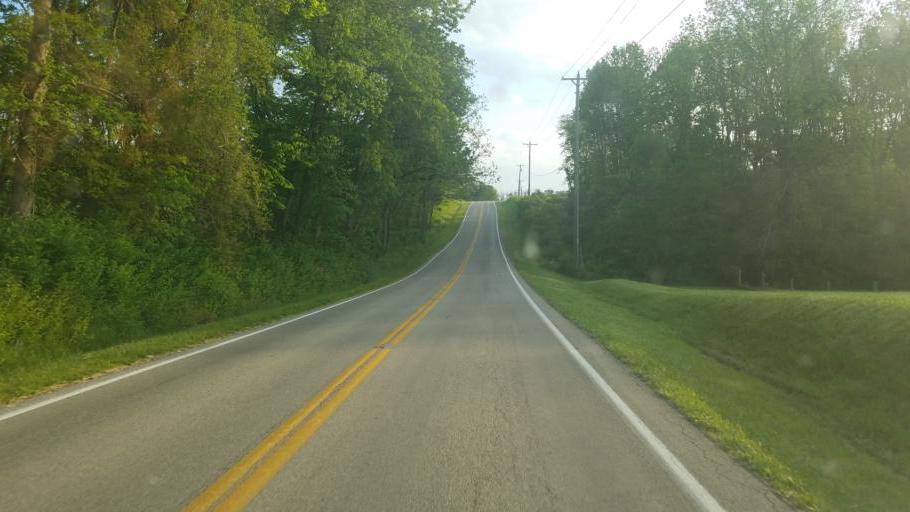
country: US
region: Ohio
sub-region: Highland County
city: Leesburg
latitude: 39.3492
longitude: -83.5884
